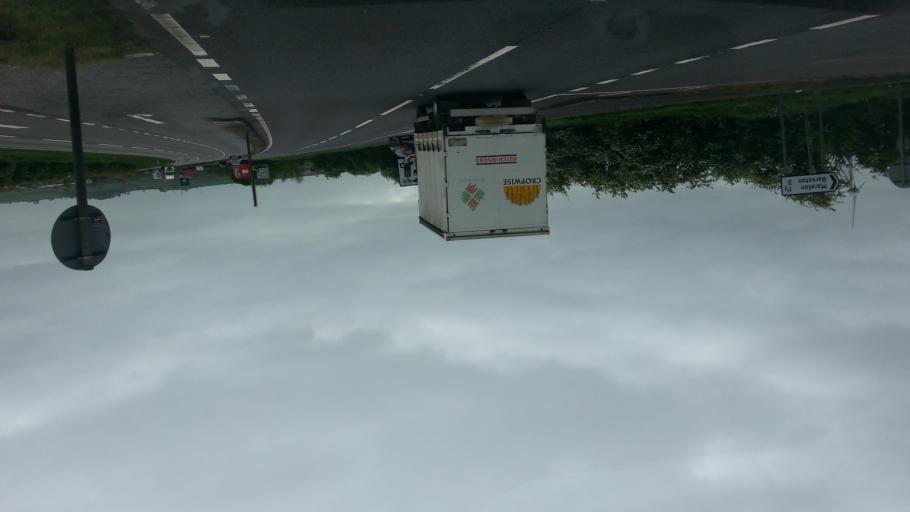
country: GB
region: England
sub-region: Lincolnshire
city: Great Gonerby
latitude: 52.9642
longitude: -0.6942
